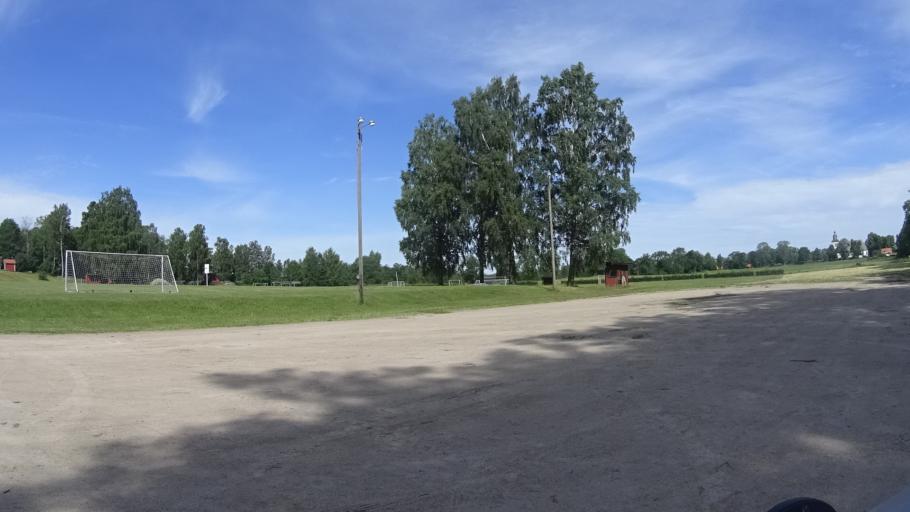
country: SE
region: Kalmar
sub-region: Vasterviks Kommun
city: Overum
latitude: 57.8914
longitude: 16.1694
